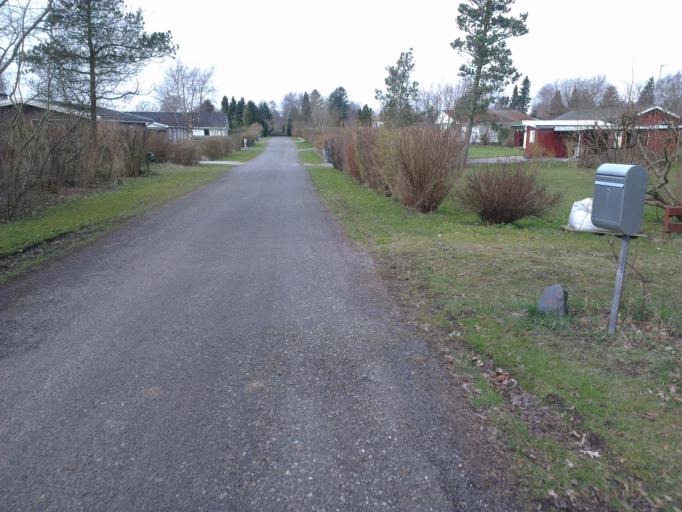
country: DK
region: Capital Region
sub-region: Frederikssund Kommune
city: Jaegerspris
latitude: 55.8104
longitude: 11.9468
